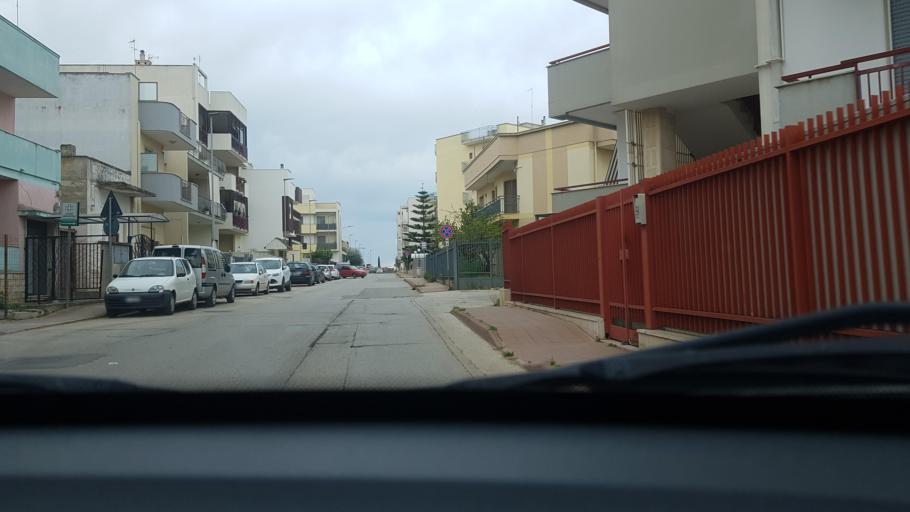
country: IT
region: Apulia
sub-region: Provincia di Bari
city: Noicattaro
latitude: 41.0323
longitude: 16.9812
